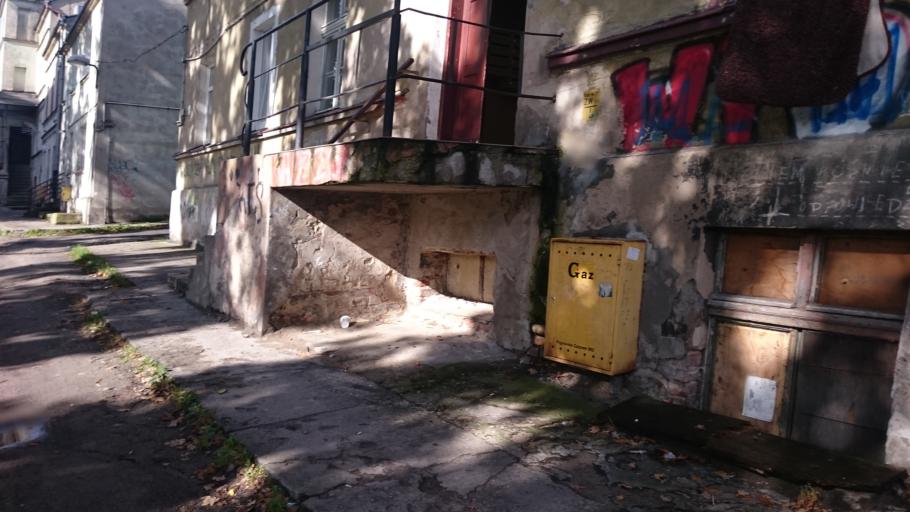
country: PL
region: Kujawsko-Pomorskie
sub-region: Grudziadz
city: Grudziadz
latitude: 53.4858
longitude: 18.7505
